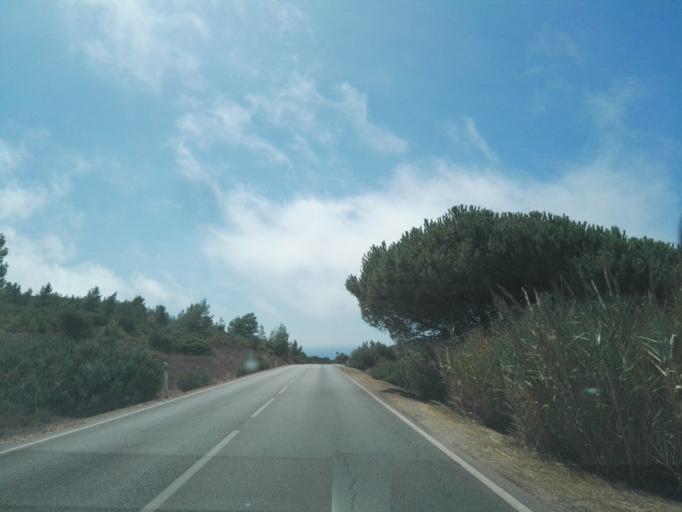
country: PT
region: Setubal
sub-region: Sesimbra
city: Sesimbra
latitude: 38.4504
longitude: -9.0889
